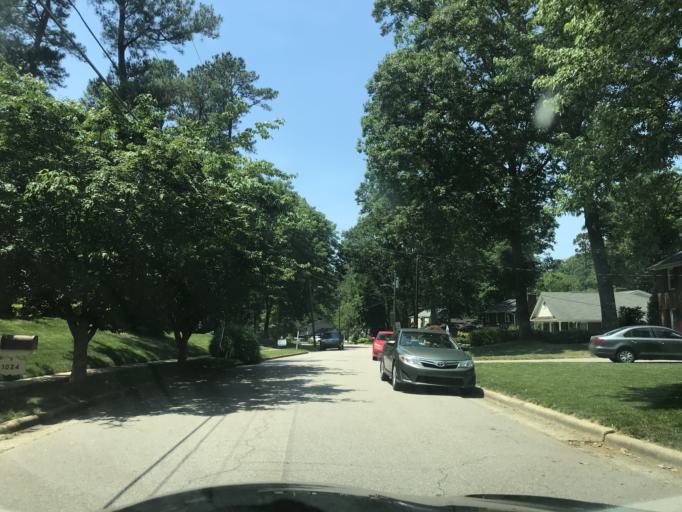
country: US
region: North Carolina
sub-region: Wake County
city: West Raleigh
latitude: 35.8493
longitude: -78.6178
